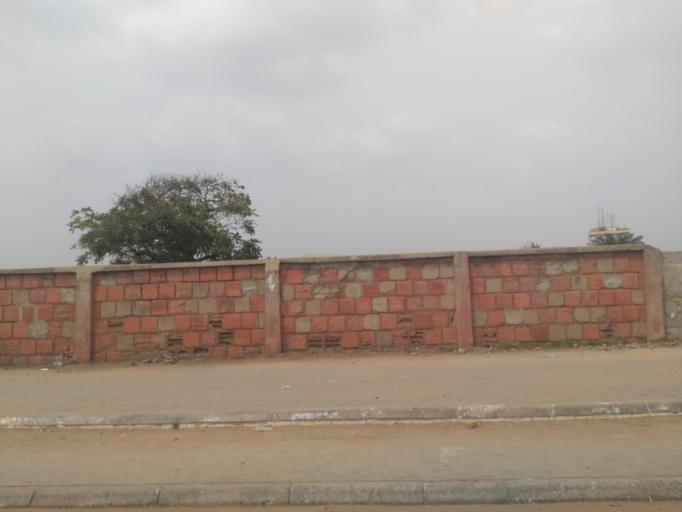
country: GH
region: Greater Accra
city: Accra
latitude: 5.5475
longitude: -0.1998
